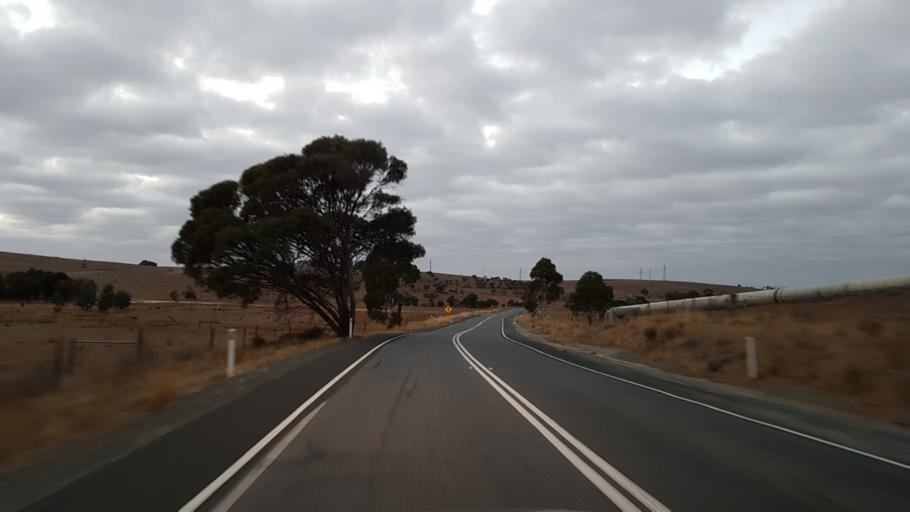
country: AU
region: South Australia
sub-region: Mount Barker
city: Callington
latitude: -35.0529
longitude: 139.0069
